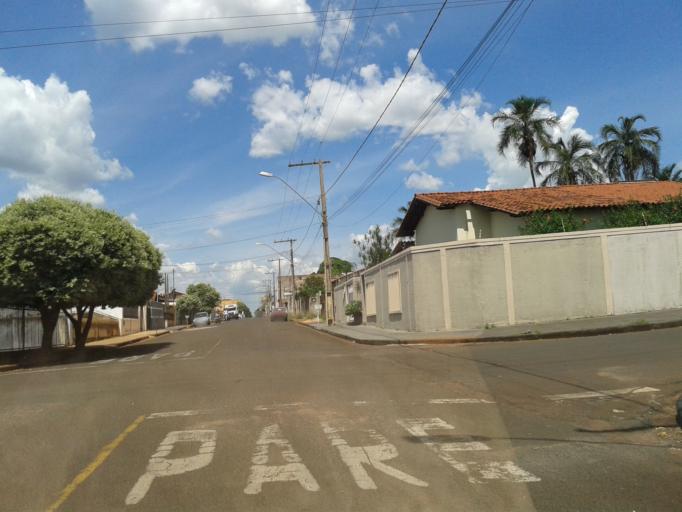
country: BR
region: Minas Gerais
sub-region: Ituiutaba
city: Ituiutaba
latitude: -18.9834
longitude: -49.4701
